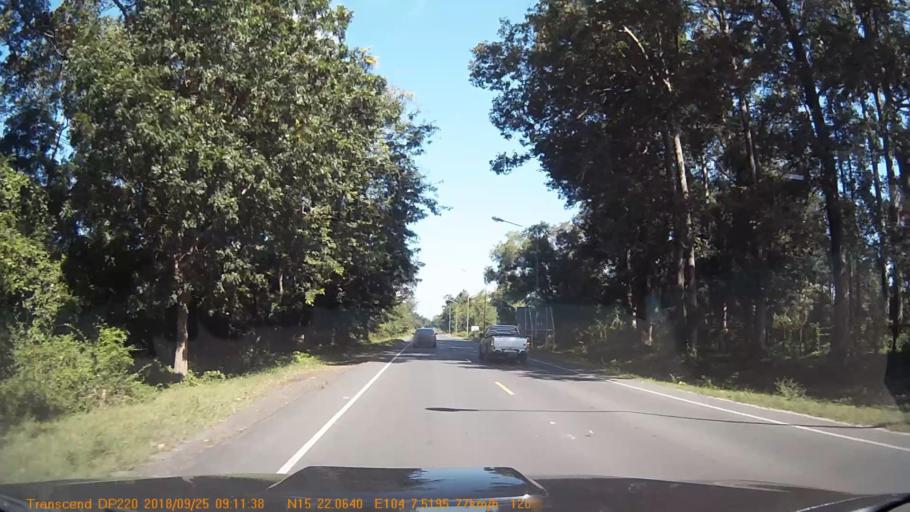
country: TH
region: Sisaket
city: Rasi Salai
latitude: 15.3677
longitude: 104.1254
